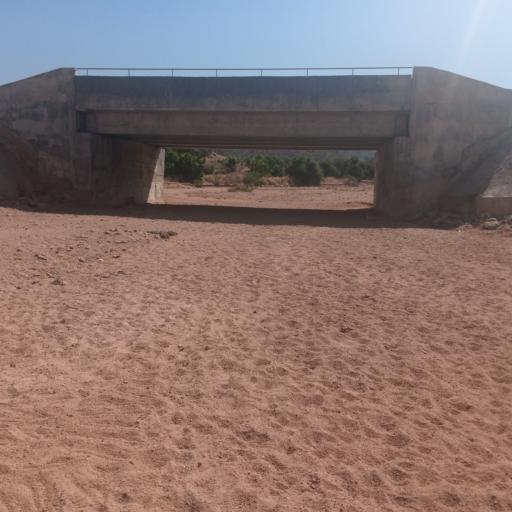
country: NG
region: Adamawa
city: Numan
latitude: 9.8025
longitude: 12.3696
